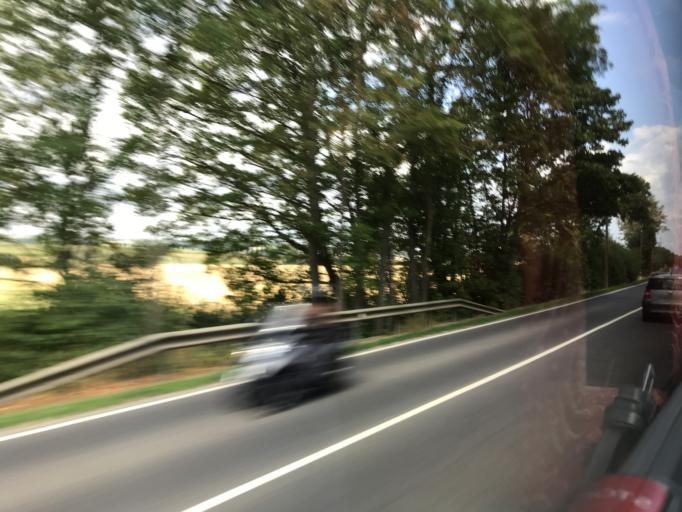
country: LU
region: Luxembourg
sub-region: Canton de Luxembourg
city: Alzingen
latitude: 49.5495
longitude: 6.1734
